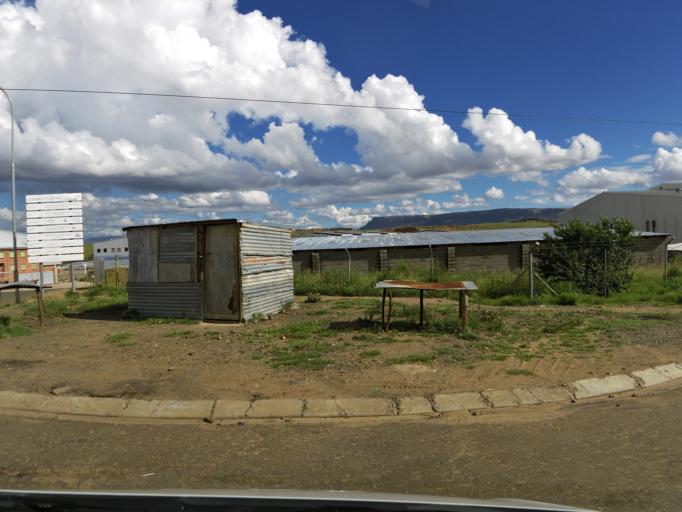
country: LS
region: Maseru
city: Maseru
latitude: -29.3797
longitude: 27.4863
